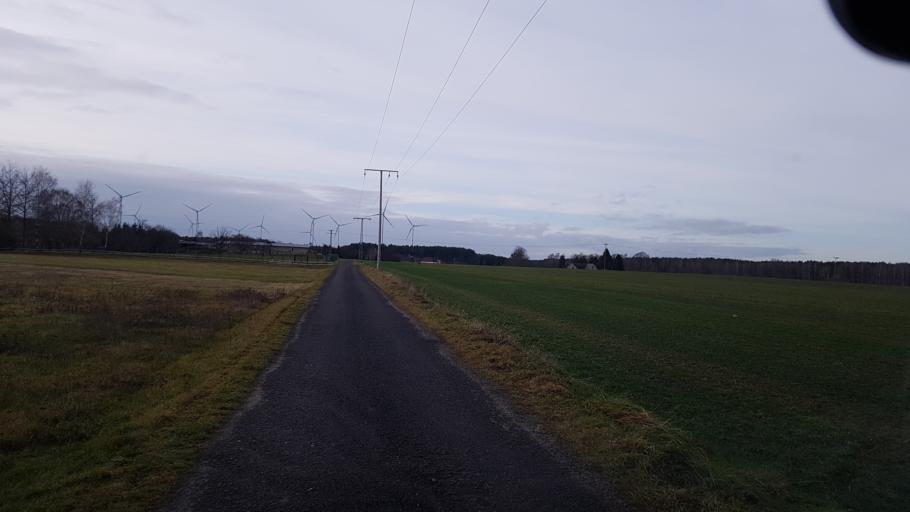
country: DE
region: Brandenburg
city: Sallgast
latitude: 51.6417
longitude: 13.8597
